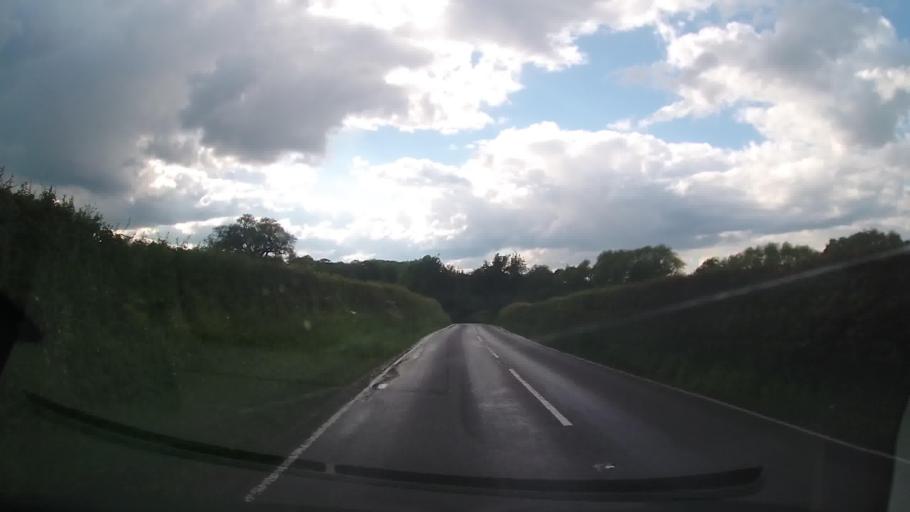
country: GB
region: England
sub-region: Shropshire
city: Berrington
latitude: 52.6772
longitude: -2.6483
